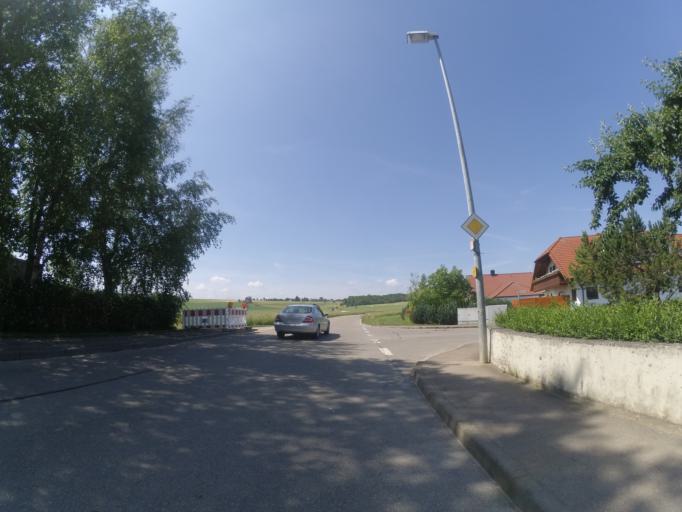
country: DE
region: Baden-Wuerttemberg
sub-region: Tuebingen Region
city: Bernstadt
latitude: 48.4836
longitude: 10.0254
